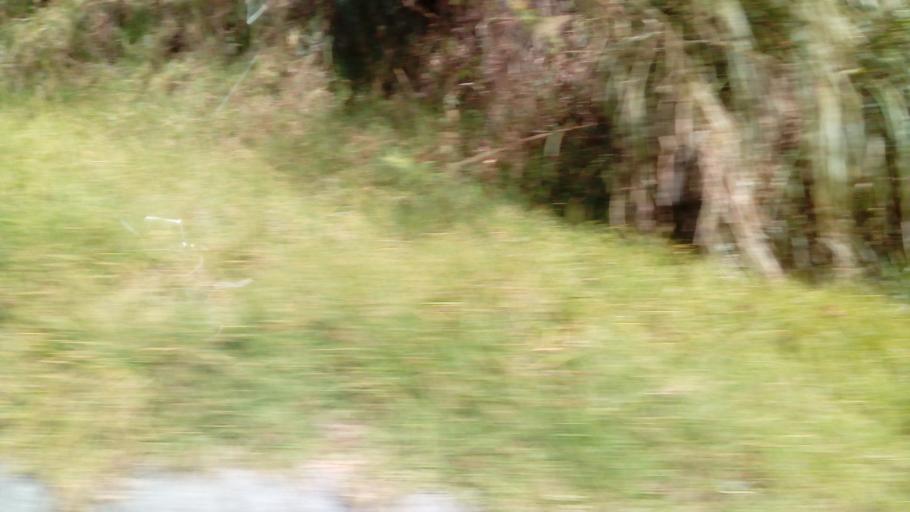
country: TW
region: Taiwan
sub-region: Hualien
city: Hualian
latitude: 24.3697
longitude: 121.3406
